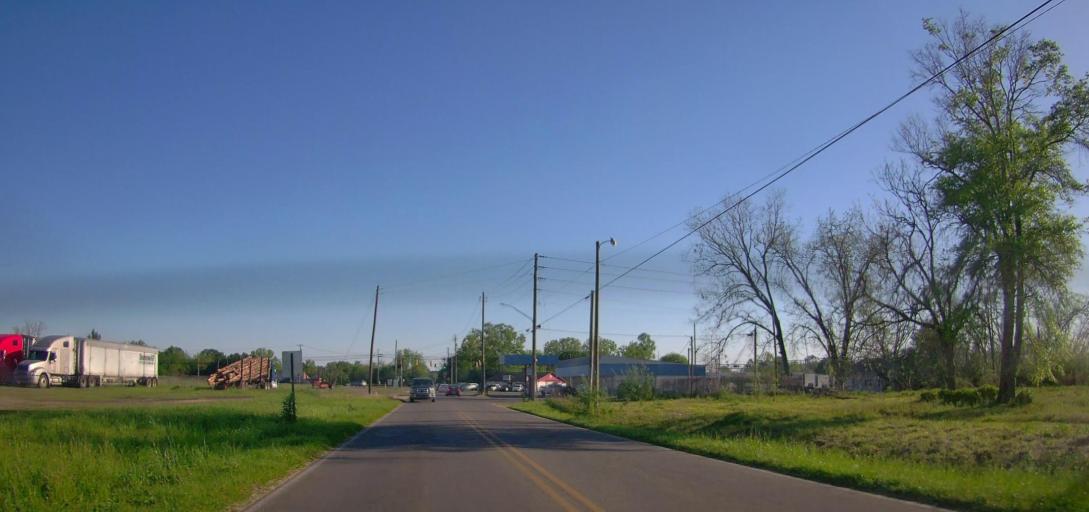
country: US
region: Georgia
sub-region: Ben Hill County
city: Fitzgerald
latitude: 31.7161
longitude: -83.2439
